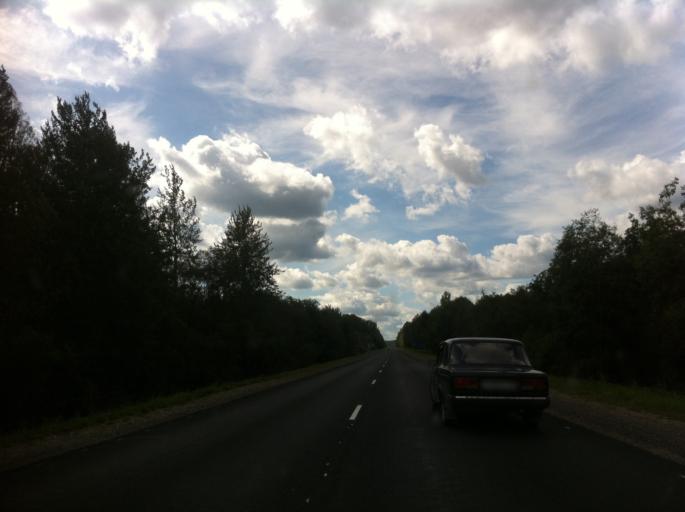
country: RU
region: Pskov
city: Izborsk
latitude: 57.7141
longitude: 27.9095
